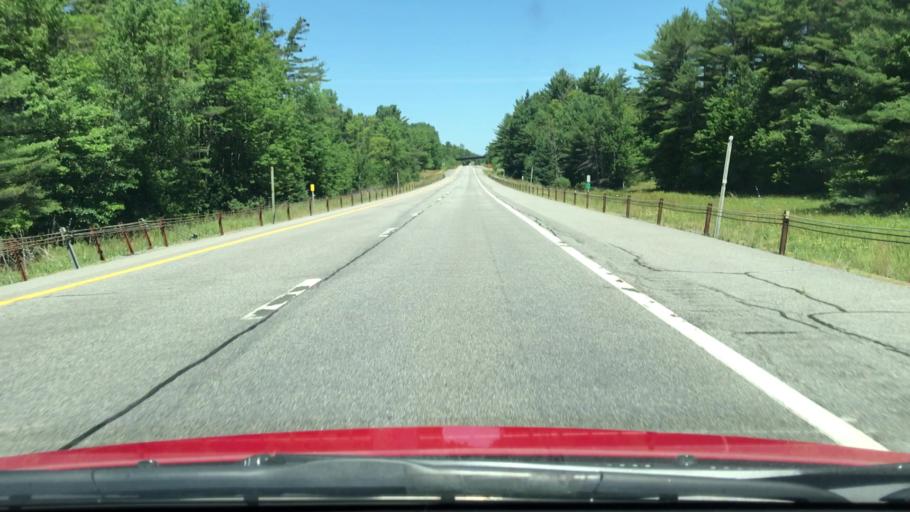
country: US
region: New York
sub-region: Essex County
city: Elizabethtown
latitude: 44.1610
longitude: -73.5832
